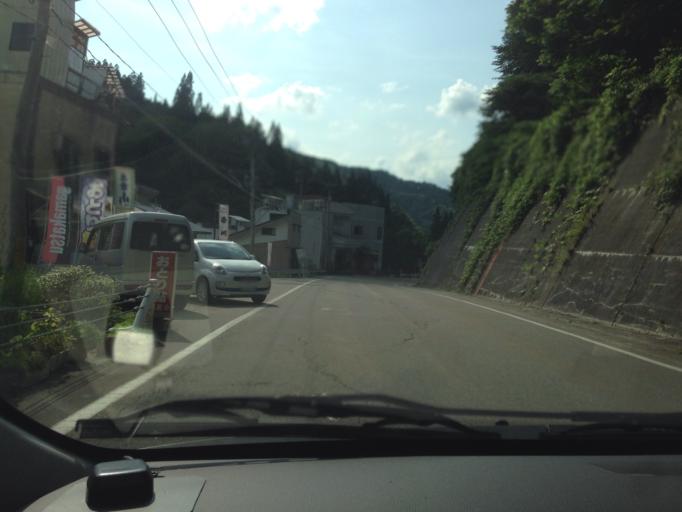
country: JP
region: Fukushima
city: Kitakata
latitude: 37.4215
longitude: 139.5458
